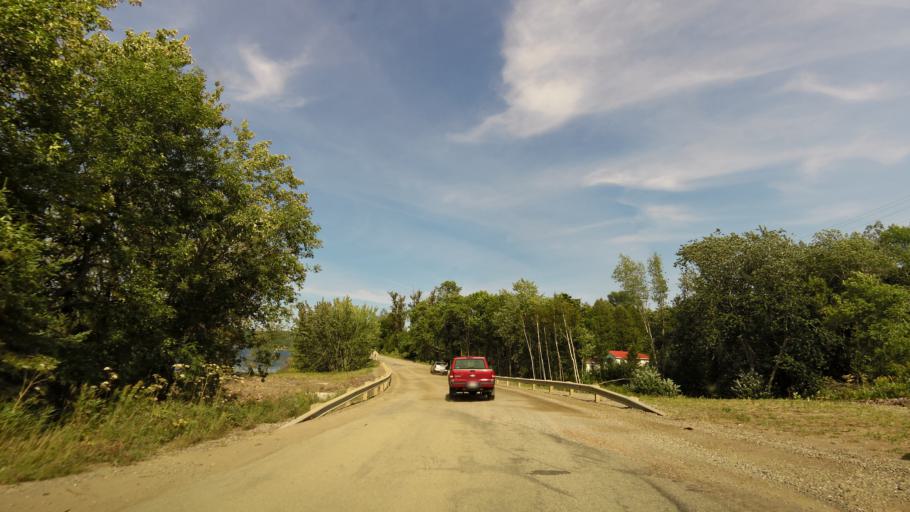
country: CA
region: New Brunswick
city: Hampton
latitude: 45.6024
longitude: -65.9094
